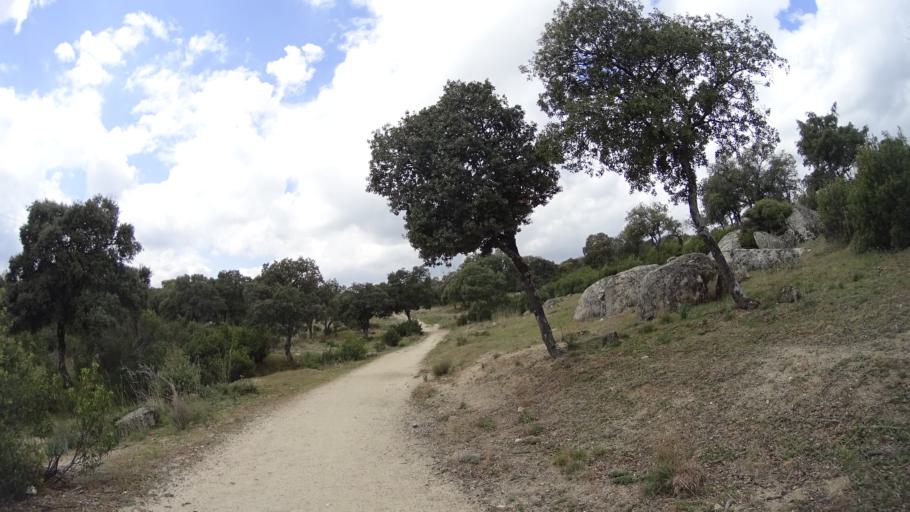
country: ES
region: Madrid
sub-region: Provincia de Madrid
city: Hoyo de Manzanares
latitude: 40.6202
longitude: -3.8884
